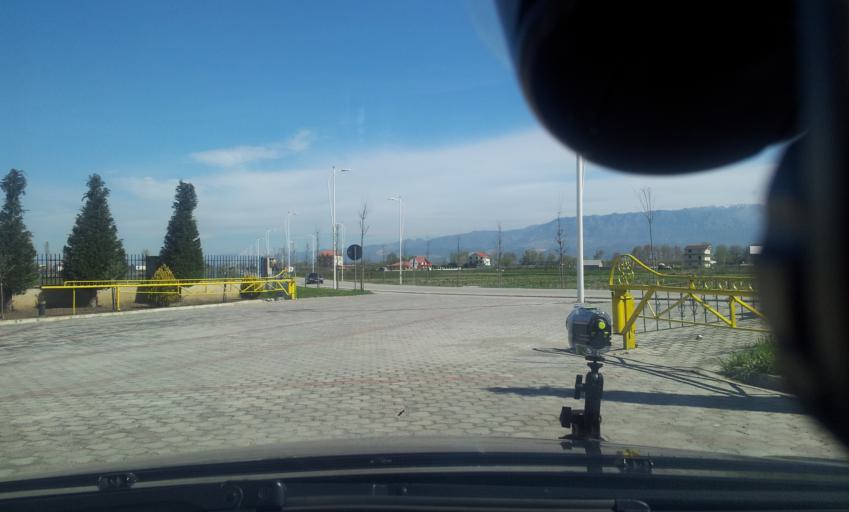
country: AL
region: Tirane
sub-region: Rrethi i Tiranes
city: Berxull
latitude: 41.3731
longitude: 19.7034
